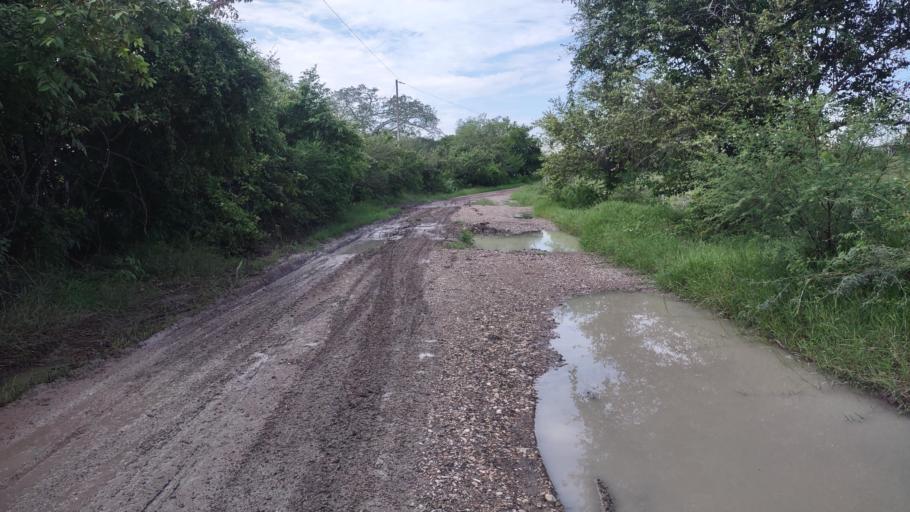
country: MX
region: Veracruz
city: El Higo
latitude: 21.7579
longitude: -98.1868
